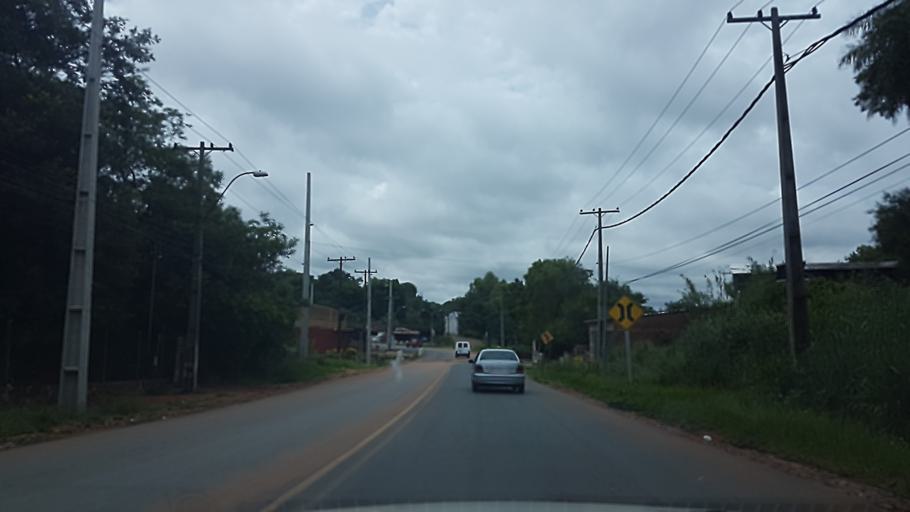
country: PY
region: Central
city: San Antonio
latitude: -25.4060
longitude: -57.5721
